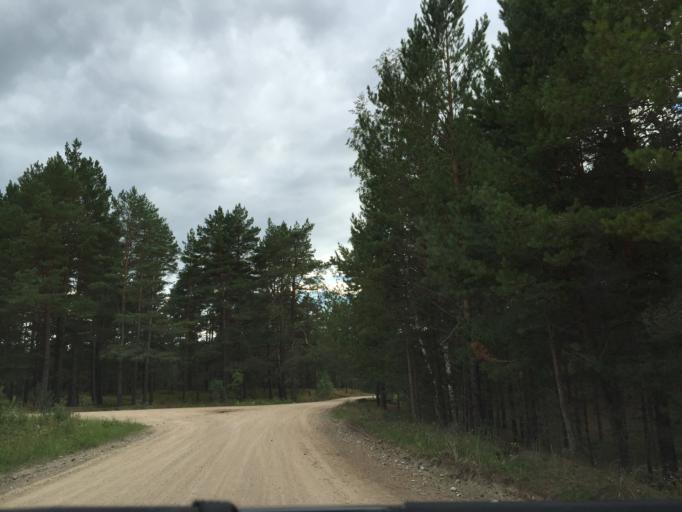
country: LV
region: Saulkrastu
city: Saulkrasti
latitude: 57.1736
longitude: 24.3801
